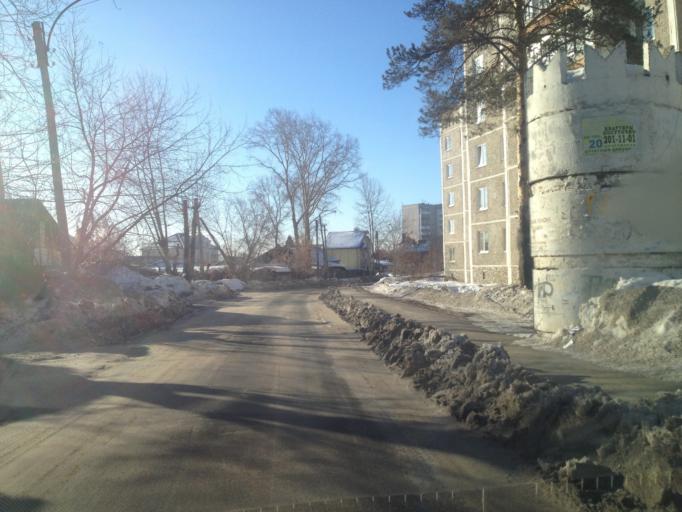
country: RU
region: Sverdlovsk
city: Sovkhoznyy
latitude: 56.7720
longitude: 60.5892
